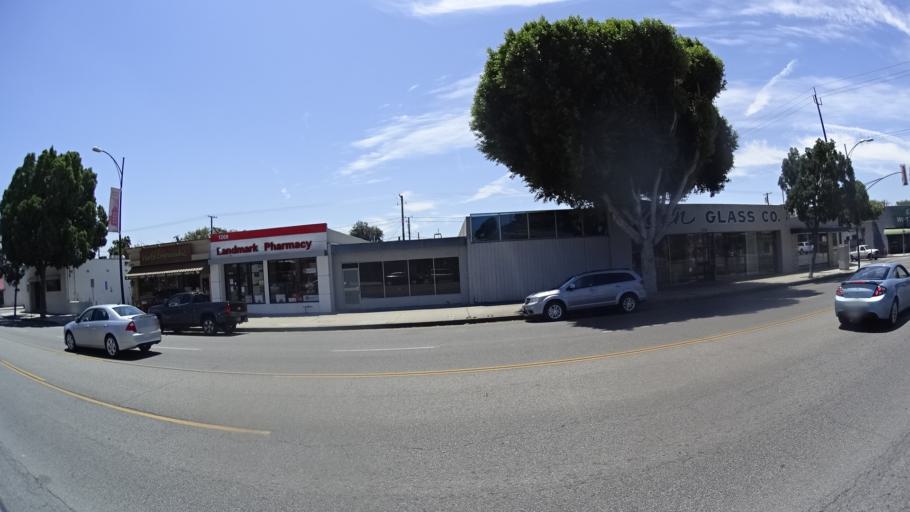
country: US
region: California
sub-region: Los Angeles County
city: Burbank
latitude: 34.1763
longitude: -118.3221
